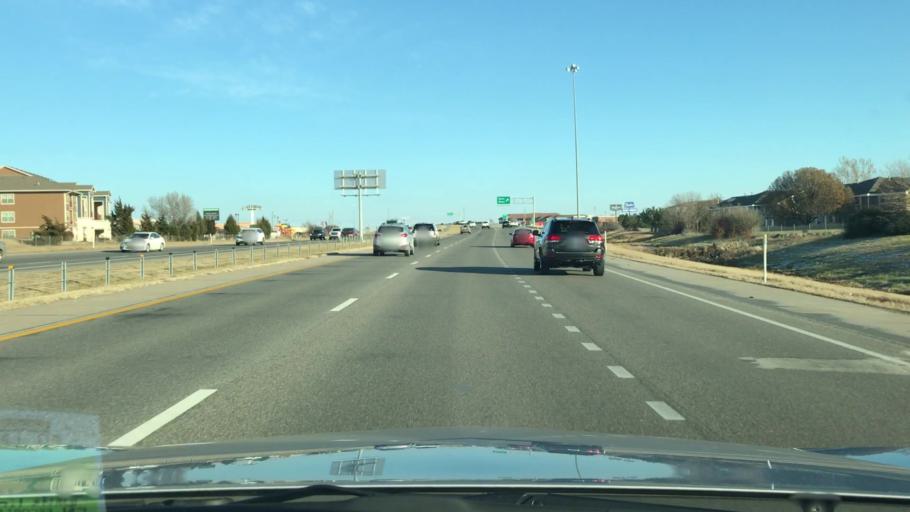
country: US
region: Kansas
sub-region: Sedgwick County
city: Bellaire
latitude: 37.7451
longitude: -97.2510
